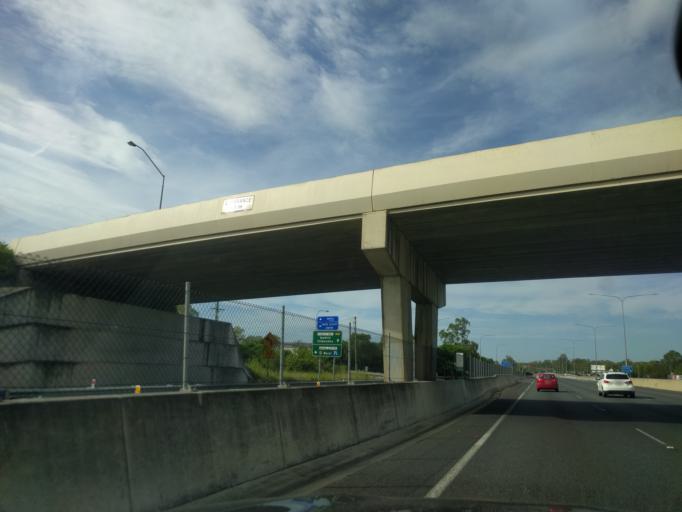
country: AU
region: Queensland
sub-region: Brisbane
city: Wacol
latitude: -27.5886
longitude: 152.9271
